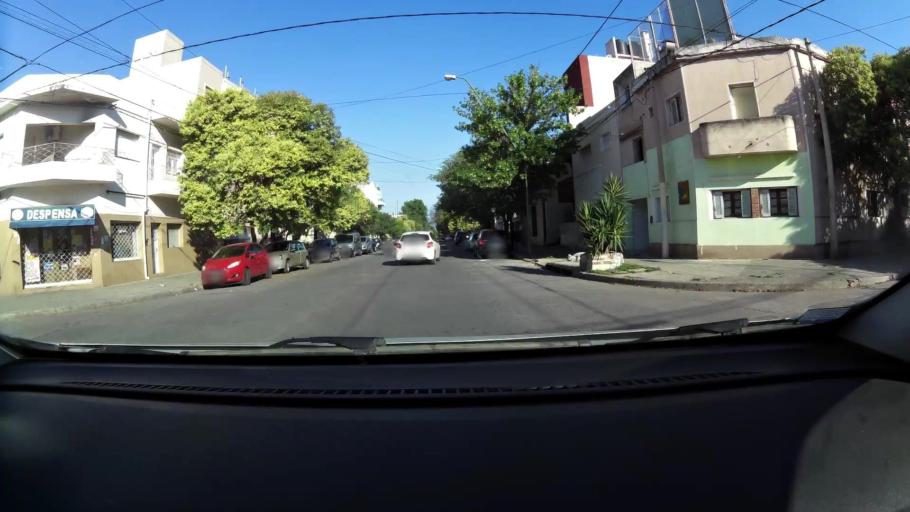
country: AR
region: Cordoba
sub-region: Departamento de Capital
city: Cordoba
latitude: -31.3932
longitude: -64.1818
